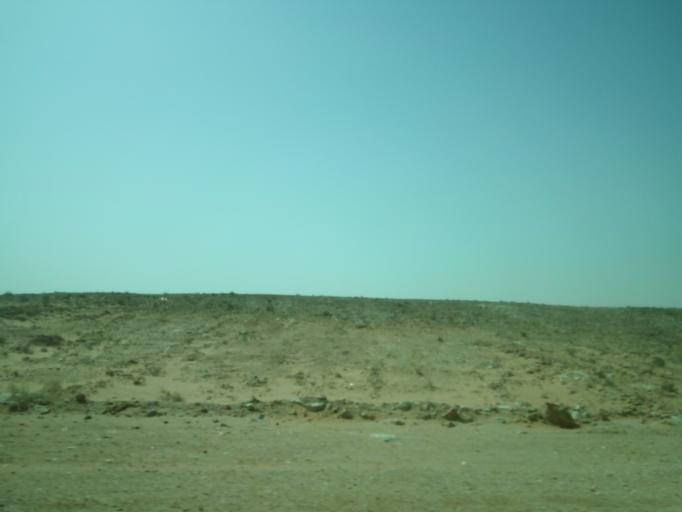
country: DZ
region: Ghardaia
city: Berriane
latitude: 32.8160
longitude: 4.1438
